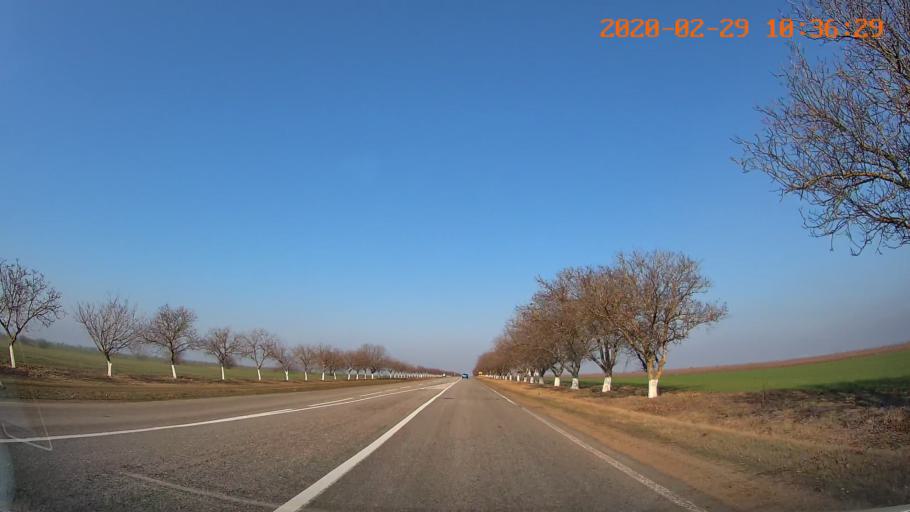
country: MD
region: Anenii Noi
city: Varnita
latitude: 46.9961
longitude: 29.5044
